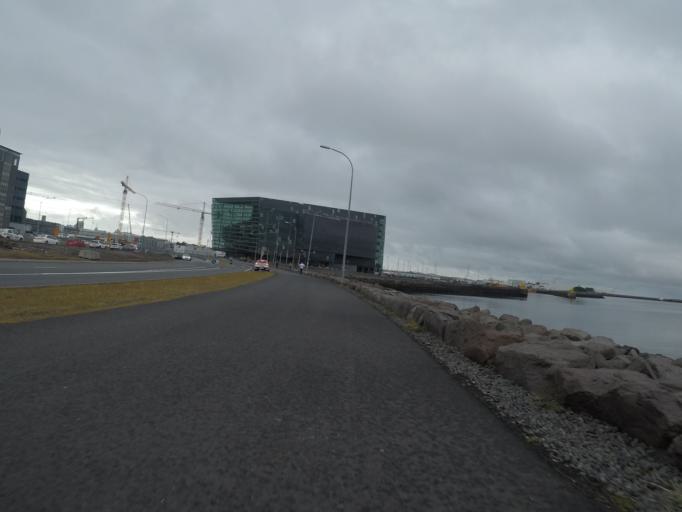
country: IS
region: Capital Region
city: Reykjavik
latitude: 64.1496
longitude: -21.9281
